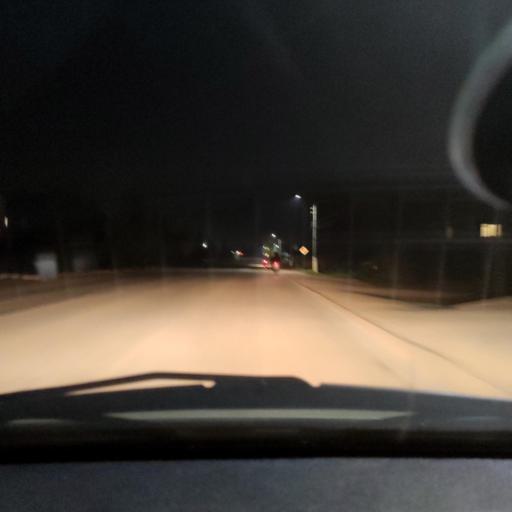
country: RU
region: Bashkortostan
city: Iglino
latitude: 54.8335
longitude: 56.4114
